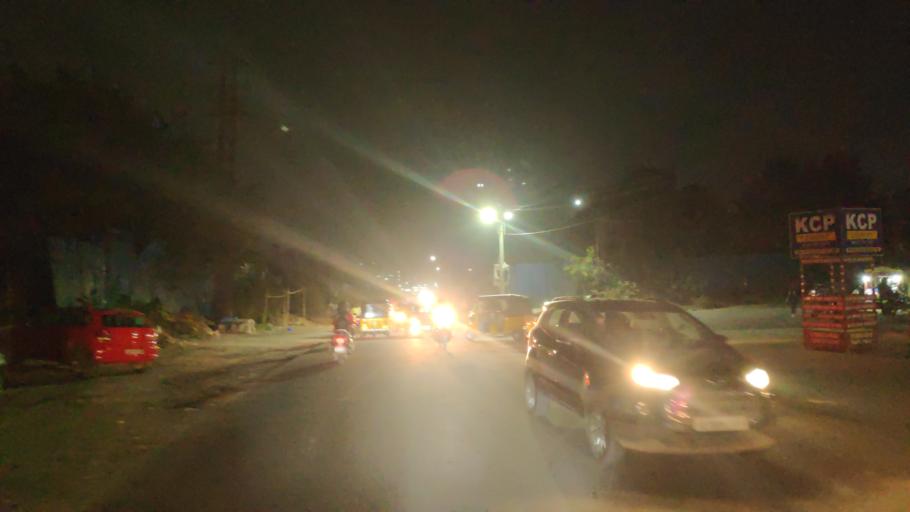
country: IN
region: Telangana
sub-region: Rangareddi
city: Kukatpalli
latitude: 17.4774
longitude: 78.3784
